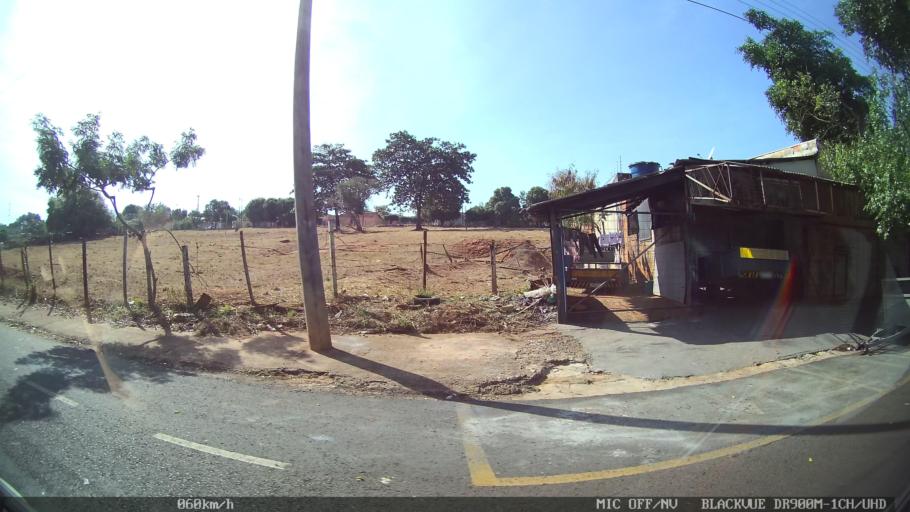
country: BR
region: Sao Paulo
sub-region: Sao Jose Do Rio Preto
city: Sao Jose do Rio Preto
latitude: -20.7907
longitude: -49.4086
